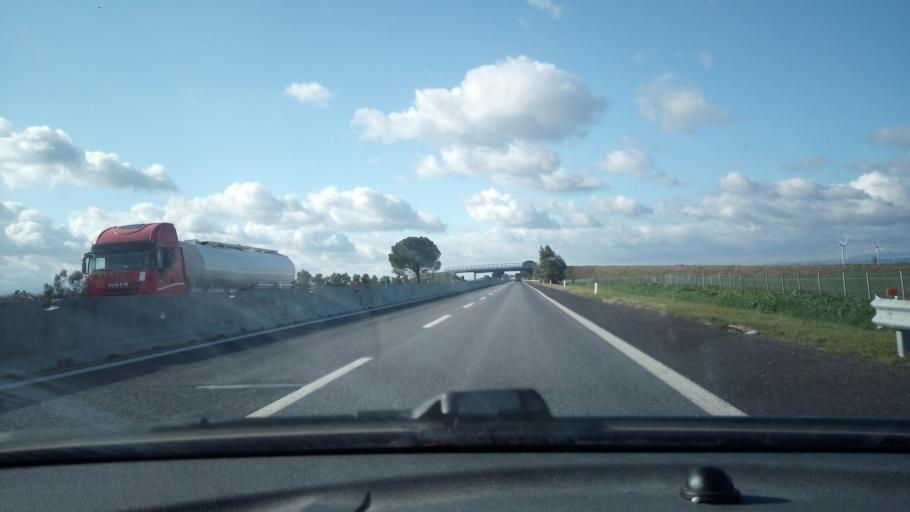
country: IT
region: Apulia
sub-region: Provincia di Foggia
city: Stornarella
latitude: 41.1898
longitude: 15.8064
